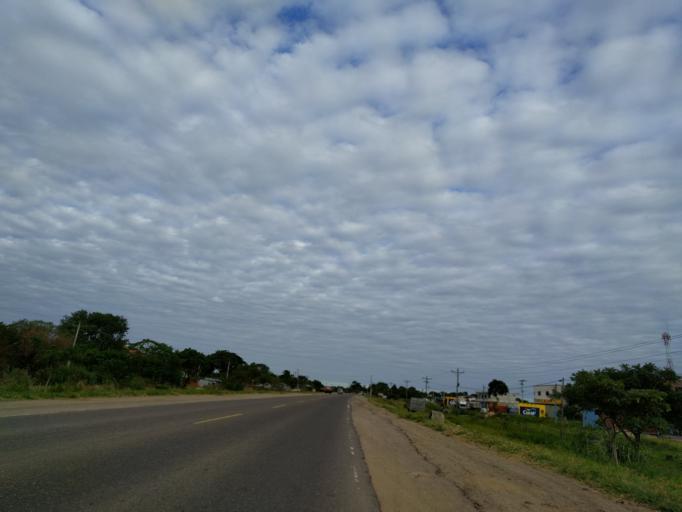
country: BO
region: Santa Cruz
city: Santa Rita
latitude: -17.8738
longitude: -63.2709
